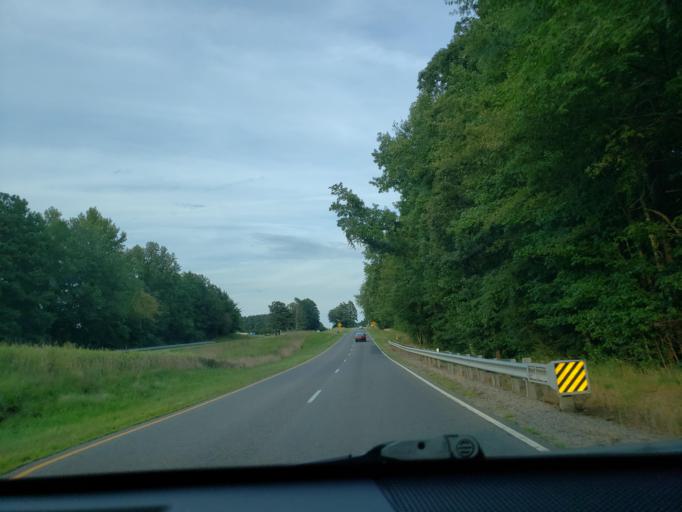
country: US
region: Virginia
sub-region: Brunswick County
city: Lawrenceville
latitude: 36.7436
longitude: -77.8837
